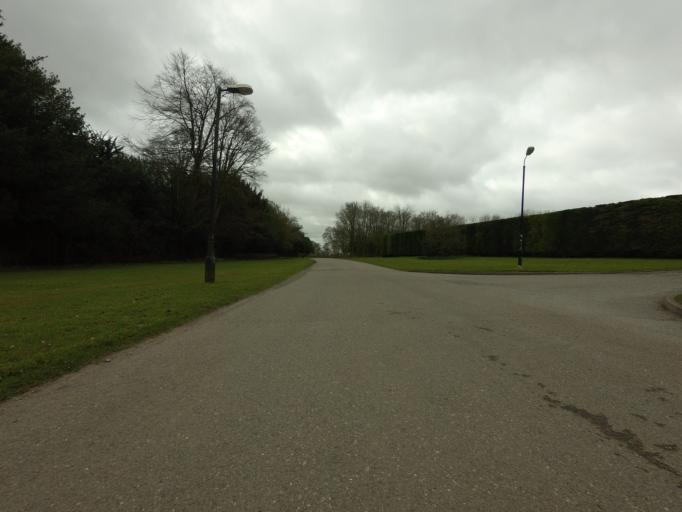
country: GB
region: England
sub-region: Lincolnshire
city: Grantham
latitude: 52.8420
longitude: -0.6409
